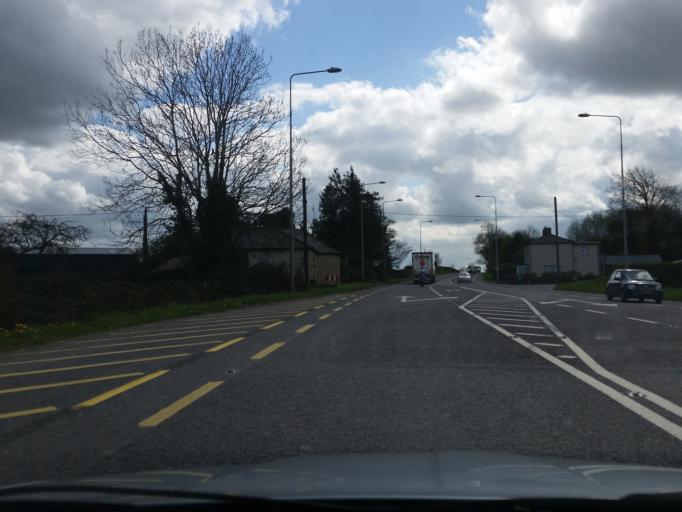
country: IE
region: Leinster
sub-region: An Mhi
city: Ratoath
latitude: 53.5720
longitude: -6.4490
